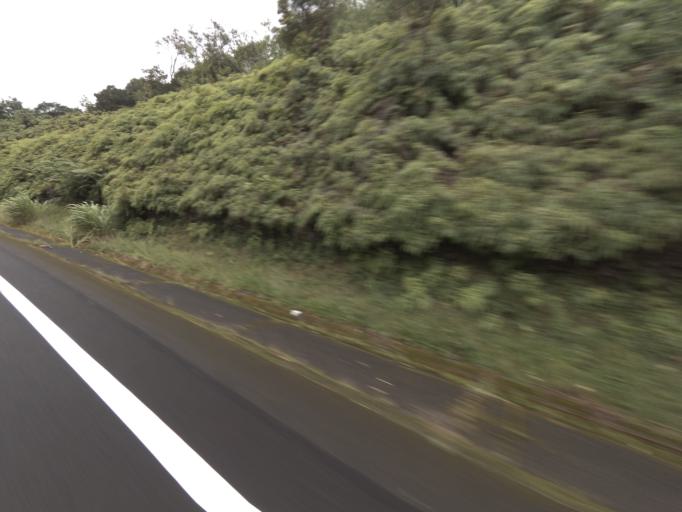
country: US
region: Hawaii
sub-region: Honolulu County
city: Kane'ohe
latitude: 21.3822
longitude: -157.8139
